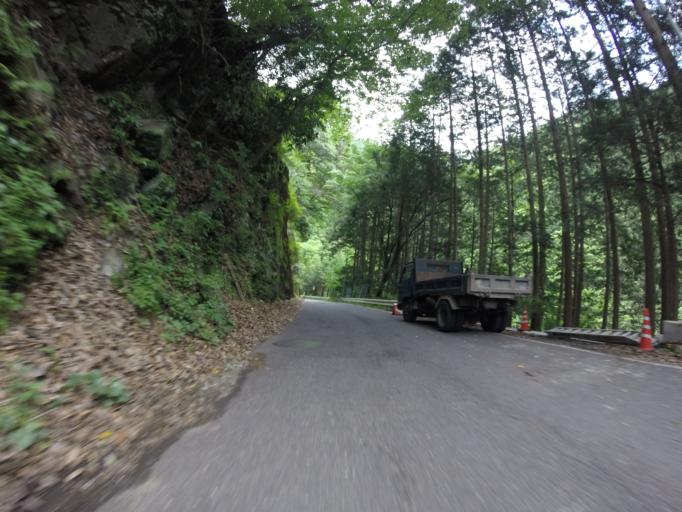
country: JP
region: Shizuoka
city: Shizuoka-shi
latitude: 35.1329
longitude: 138.2981
